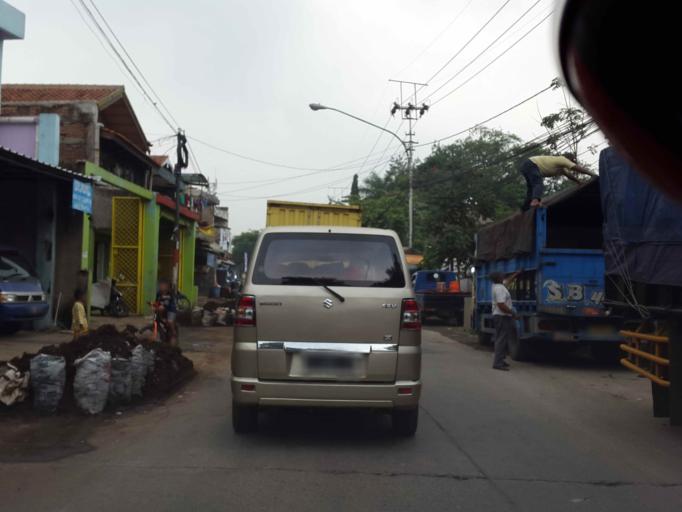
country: ID
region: West Java
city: Cimahi
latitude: -6.8995
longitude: 107.5501
